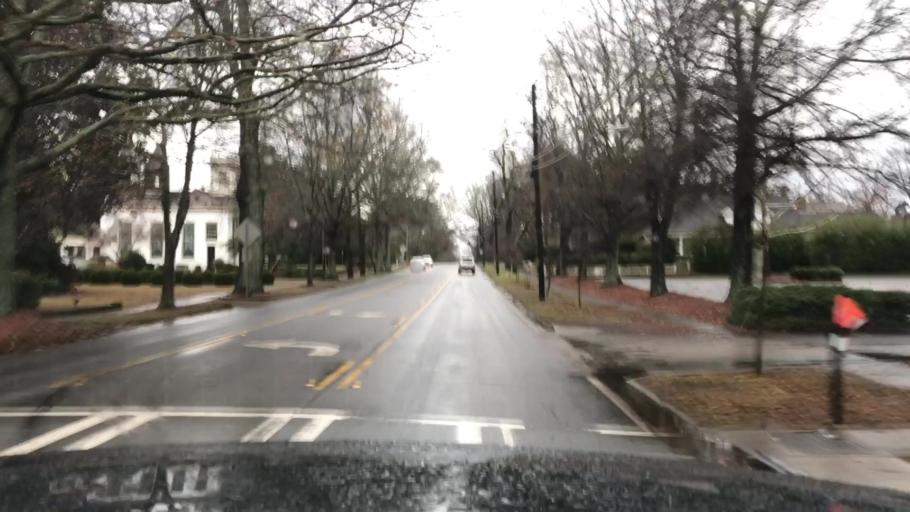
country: US
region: Georgia
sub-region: Morgan County
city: Madison
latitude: 33.5935
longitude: -83.4703
